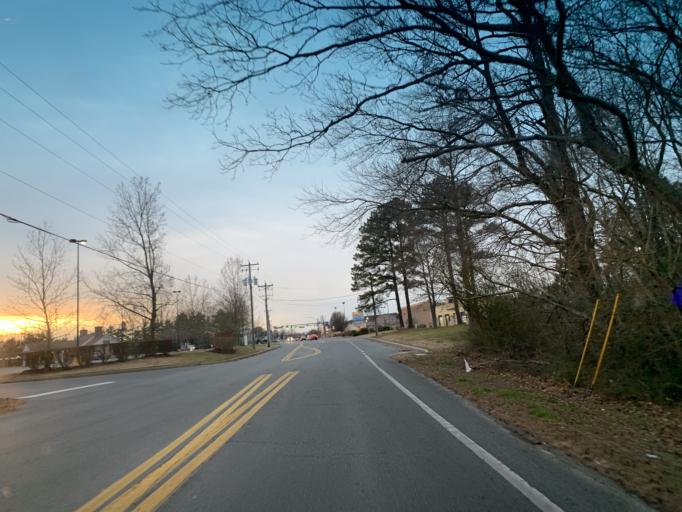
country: US
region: Maryland
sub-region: Worcester County
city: Pocomoke City
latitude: 38.0750
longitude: -75.5535
